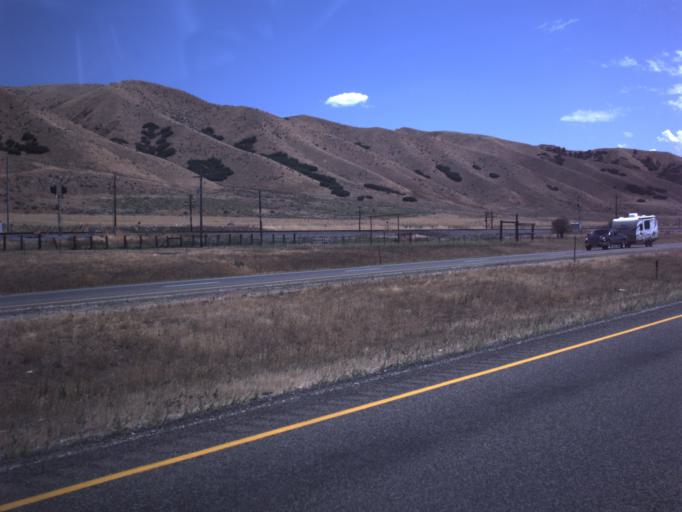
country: US
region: Utah
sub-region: Summit County
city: Coalville
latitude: 40.9923
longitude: -111.4592
